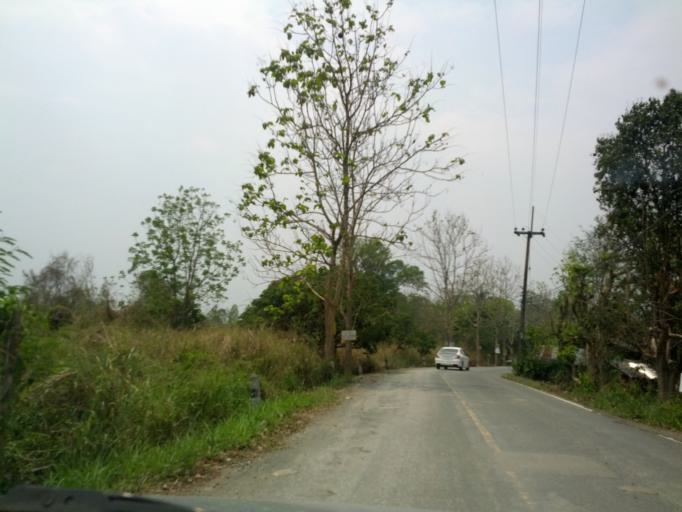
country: TH
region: Chiang Mai
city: San Sai
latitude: 18.9180
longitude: 99.0304
